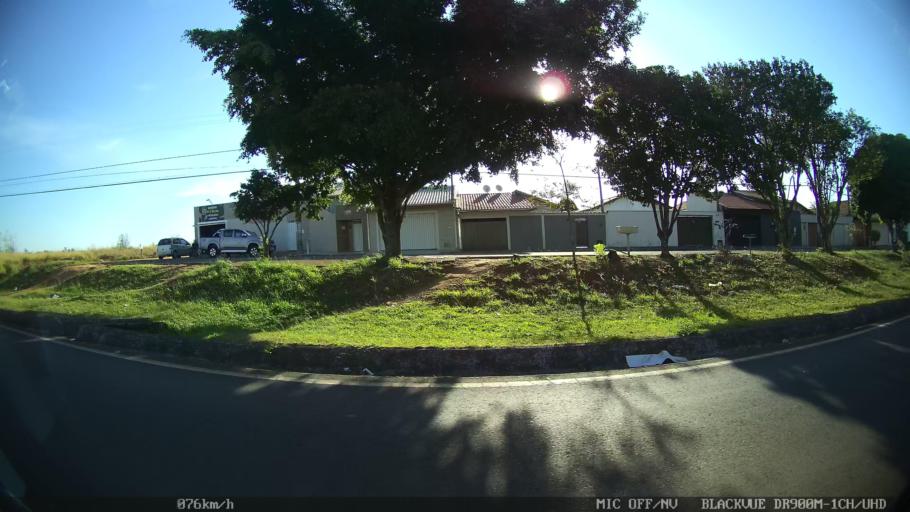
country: BR
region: Sao Paulo
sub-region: Franca
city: Franca
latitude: -20.5054
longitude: -47.3712
